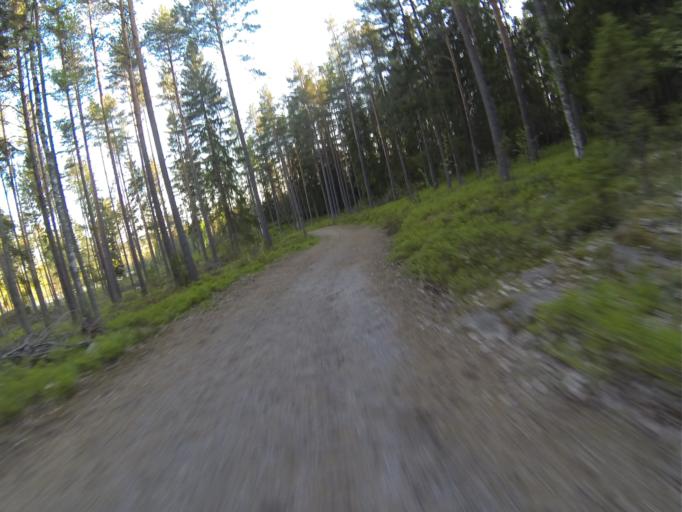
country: FI
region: Varsinais-Suomi
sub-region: Salo
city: Salo
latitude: 60.3836
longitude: 23.1796
